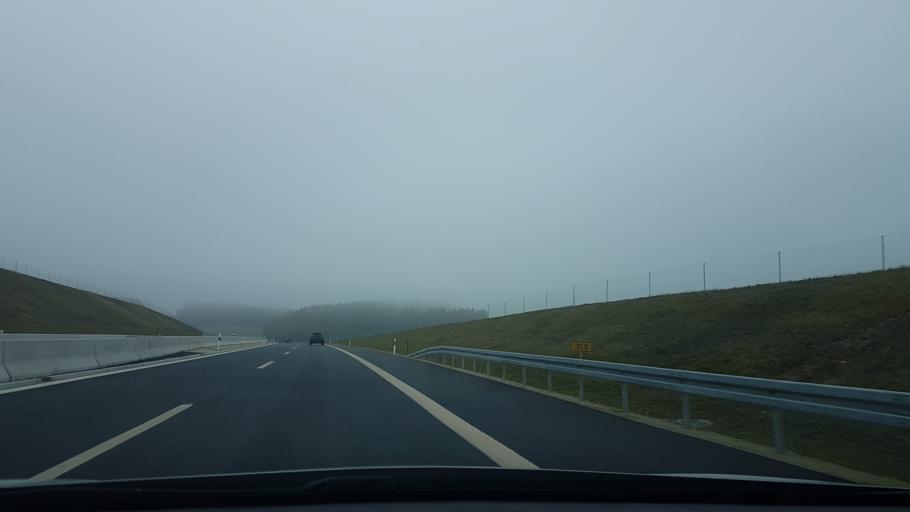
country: DE
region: Bavaria
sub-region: Lower Bavaria
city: Essenbach
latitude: 48.6417
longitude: 12.2019
